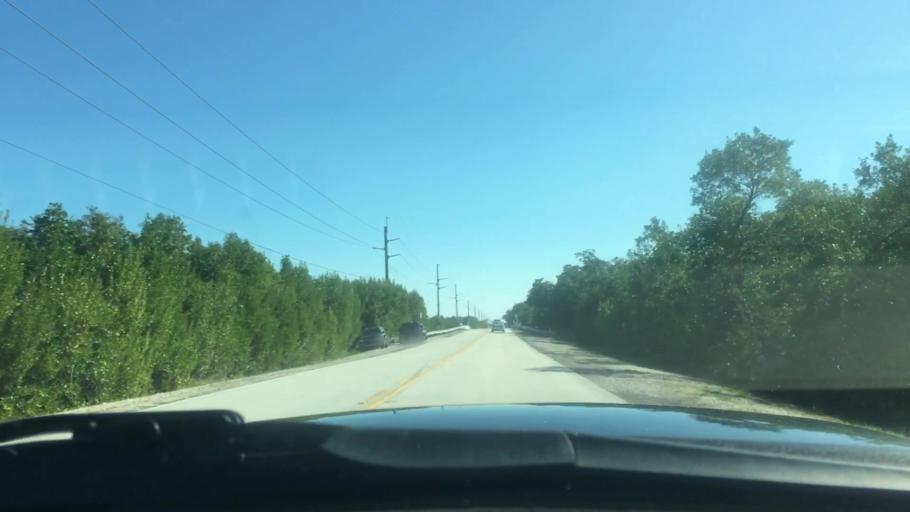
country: US
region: Florida
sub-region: Monroe County
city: North Key Largo
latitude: 25.2843
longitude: -80.3600
